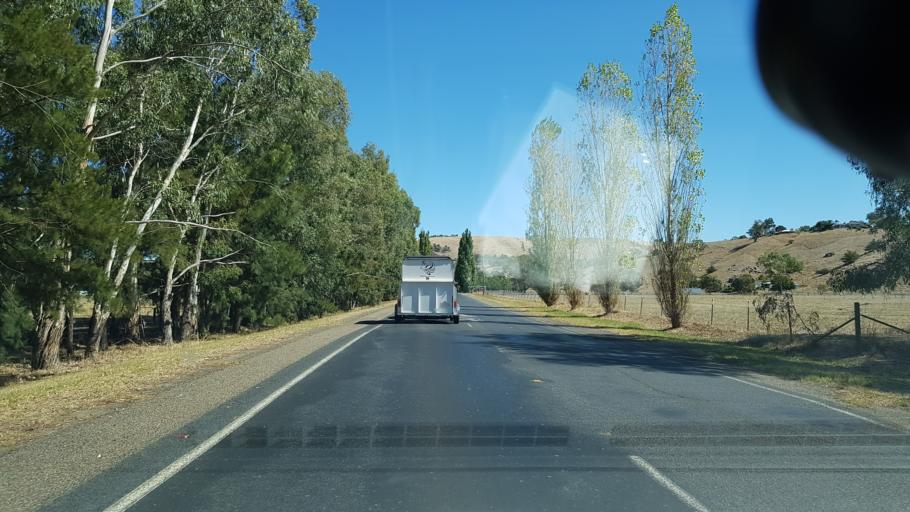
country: AU
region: New South Wales
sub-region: Gundagai
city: Gundagai
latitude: -34.8229
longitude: 148.3346
